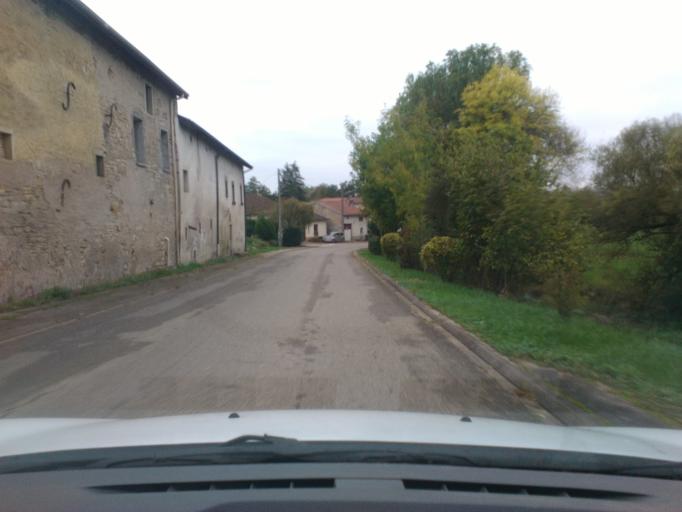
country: FR
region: Lorraine
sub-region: Departement des Vosges
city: Chavelot
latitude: 48.2812
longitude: 6.4748
